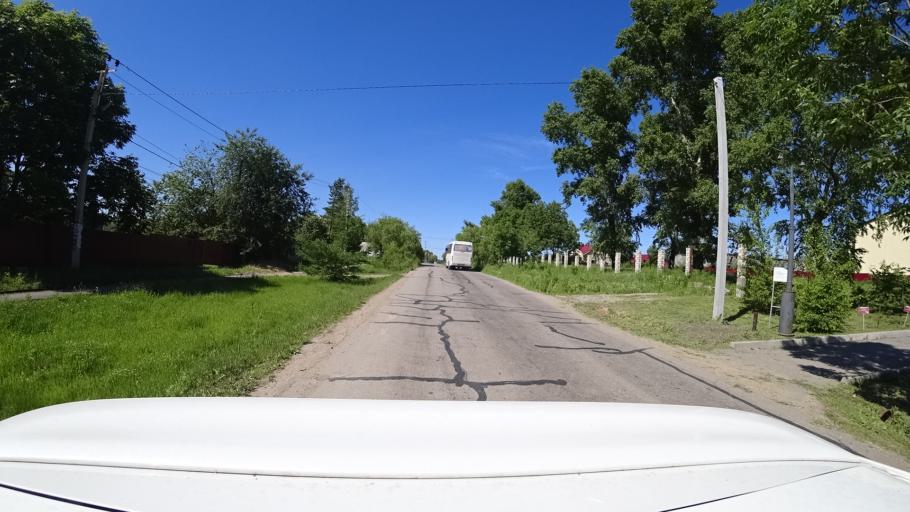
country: RU
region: Khabarovsk Krai
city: Topolevo
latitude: 48.5545
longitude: 135.1912
